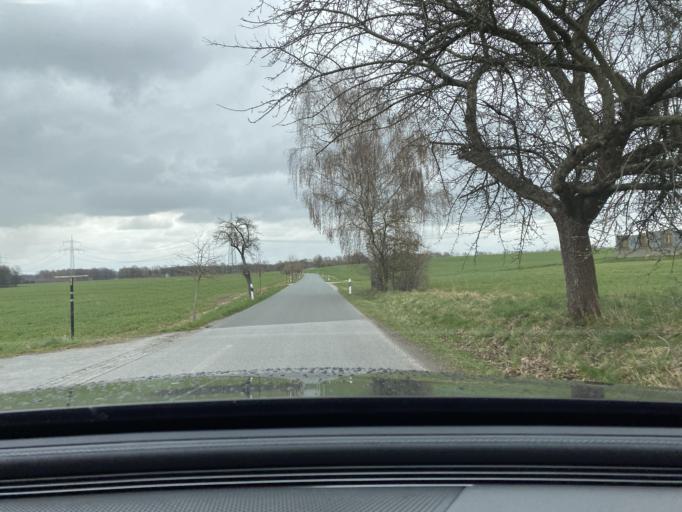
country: DE
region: Saxony
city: Radibor
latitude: 51.2492
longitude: 14.3687
